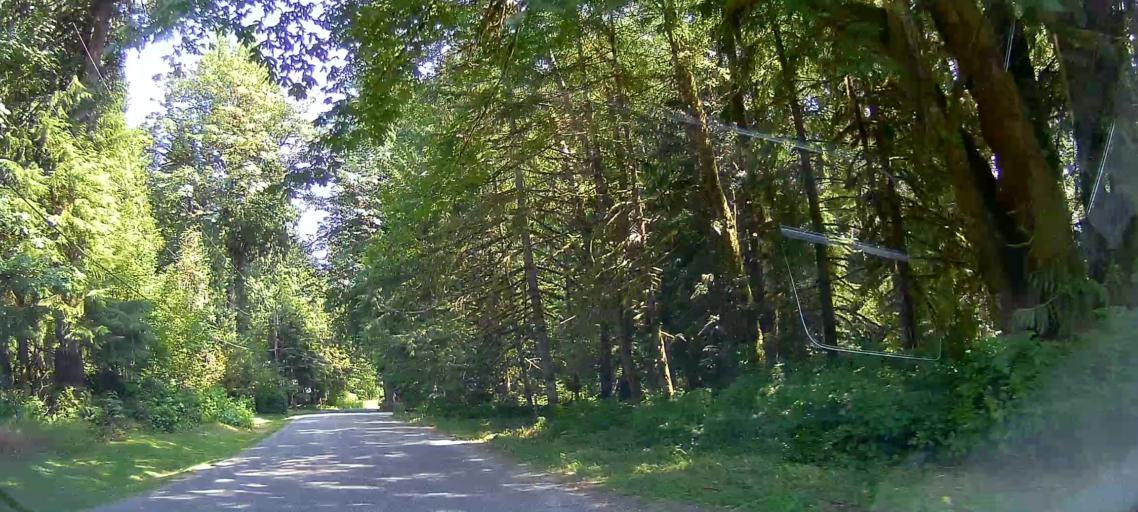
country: US
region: Washington
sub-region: Snohomish County
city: Arlington Heights
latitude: 48.3324
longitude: -122.0147
